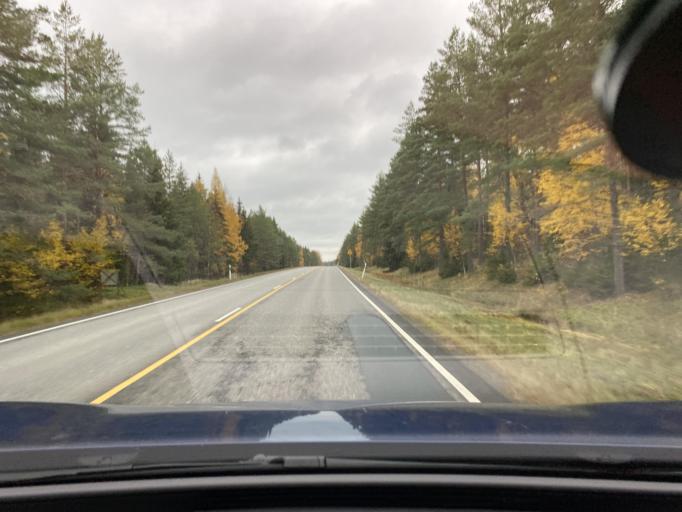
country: FI
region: Varsinais-Suomi
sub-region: Loimaa
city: Ylaene
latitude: 60.9073
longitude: 22.4100
